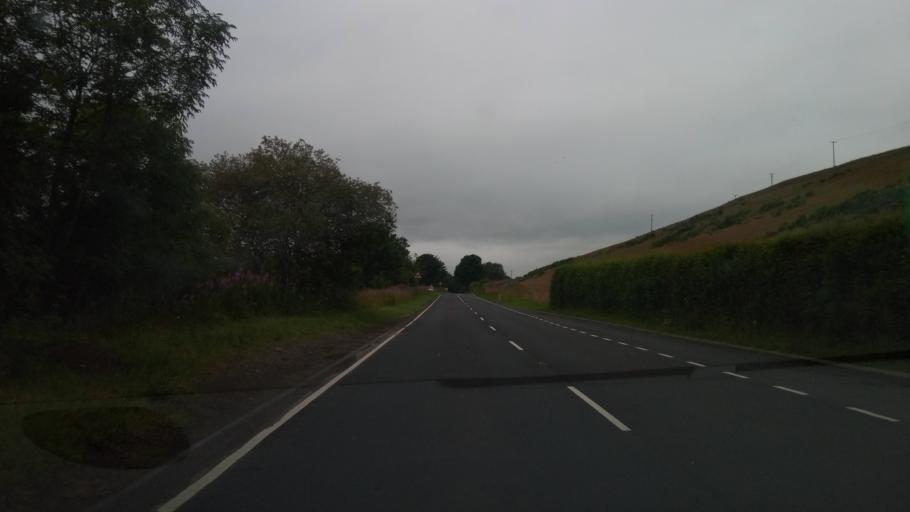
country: GB
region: Scotland
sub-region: The Scottish Borders
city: Hawick
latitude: 55.3807
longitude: -2.8707
